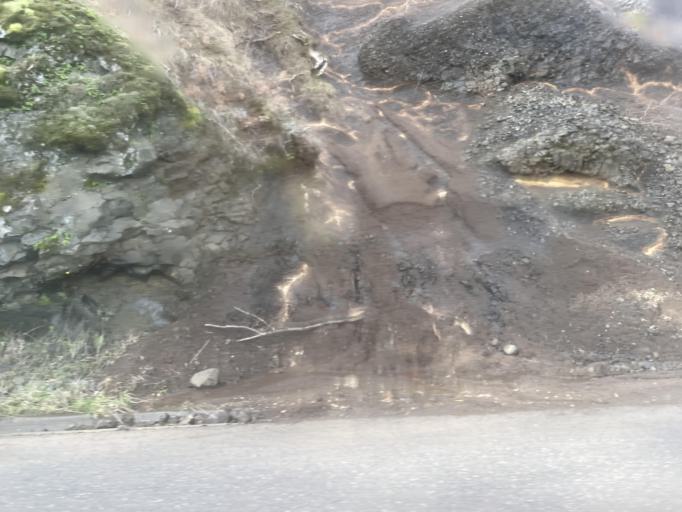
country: US
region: Washington
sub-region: Clark County
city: Washougal
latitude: 45.5372
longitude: -122.2389
